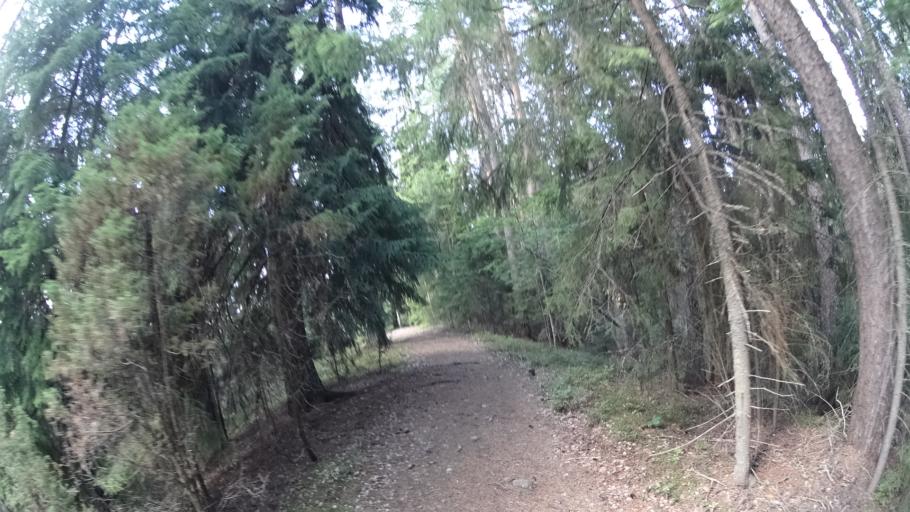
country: FI
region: Haeme
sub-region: Forssa
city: Tammela
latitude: 60.7749
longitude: 23.8403
